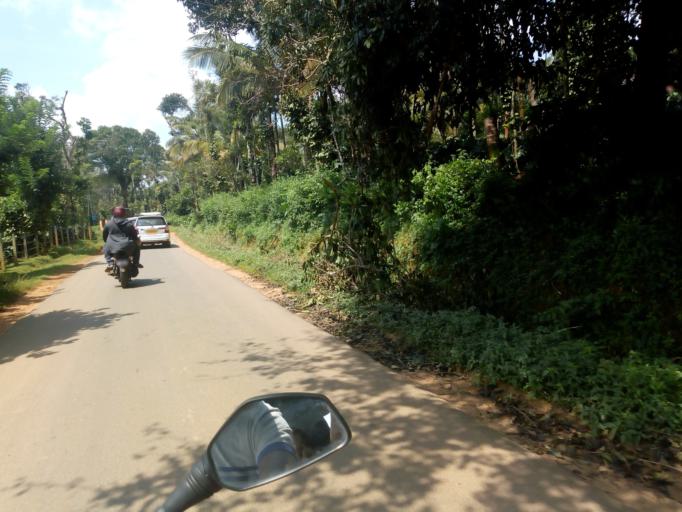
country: IN
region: Karnataka
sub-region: Kodagu
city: Ponnampet
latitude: 12.0305
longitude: 75.9635
